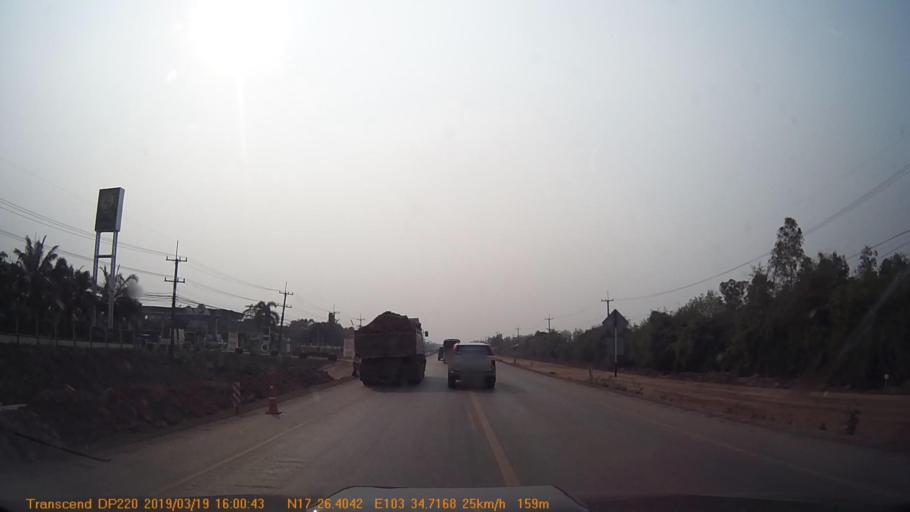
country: TH
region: Sakon Nakhon
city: Sawang Daen Din
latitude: 17.4401
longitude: 103.5785
